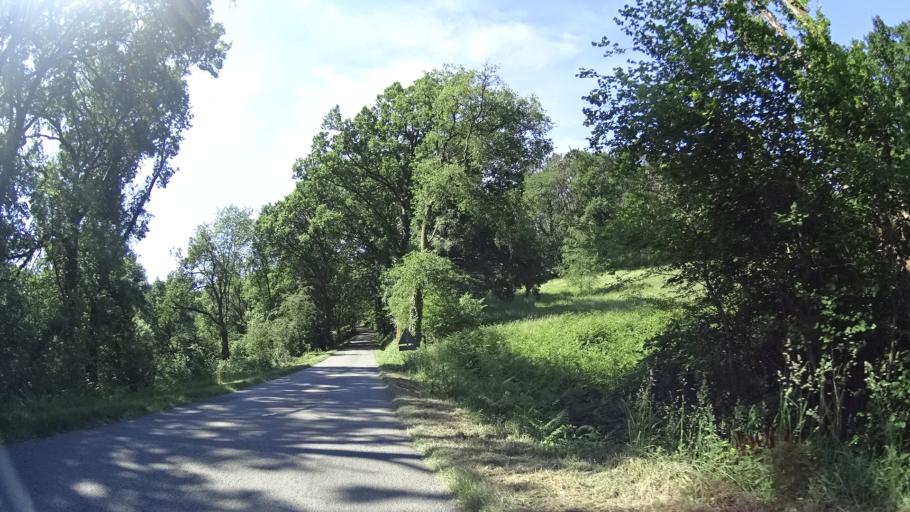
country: FR
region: Brittany
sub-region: Departement d'Ille-et-Vilaine
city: Langon
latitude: 47.7686
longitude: -1.8475
